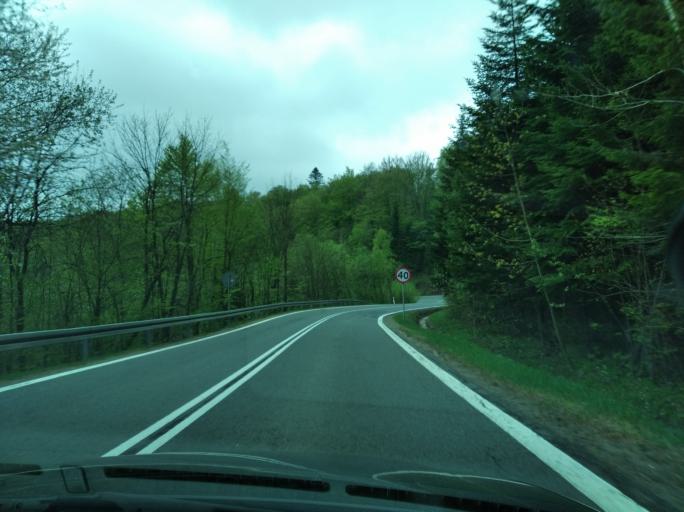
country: PL
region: Subcarpathian Voivodeship
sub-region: Powiat sanocki
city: Tyrawa Woloska
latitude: 49.5576
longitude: 22.3362
